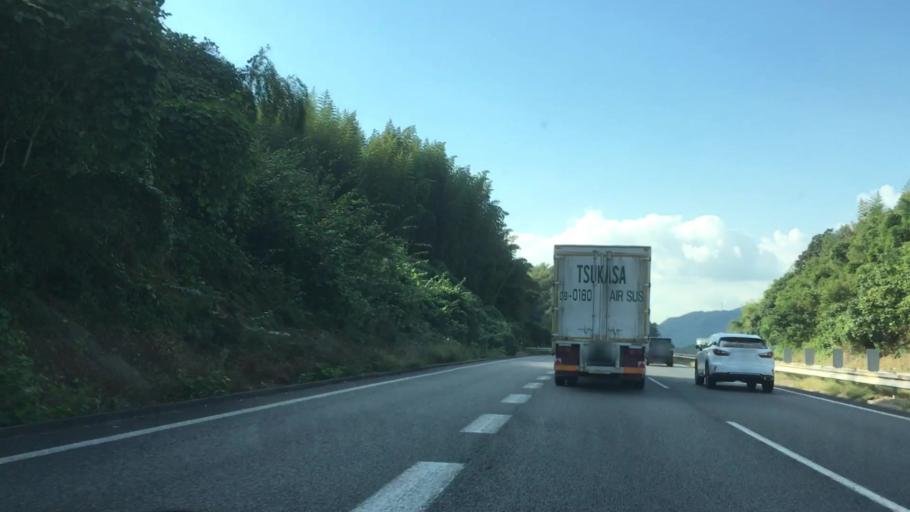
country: JP
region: Yamaguchi
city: Kudamatsu
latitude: 34.0325
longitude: 131.9330
